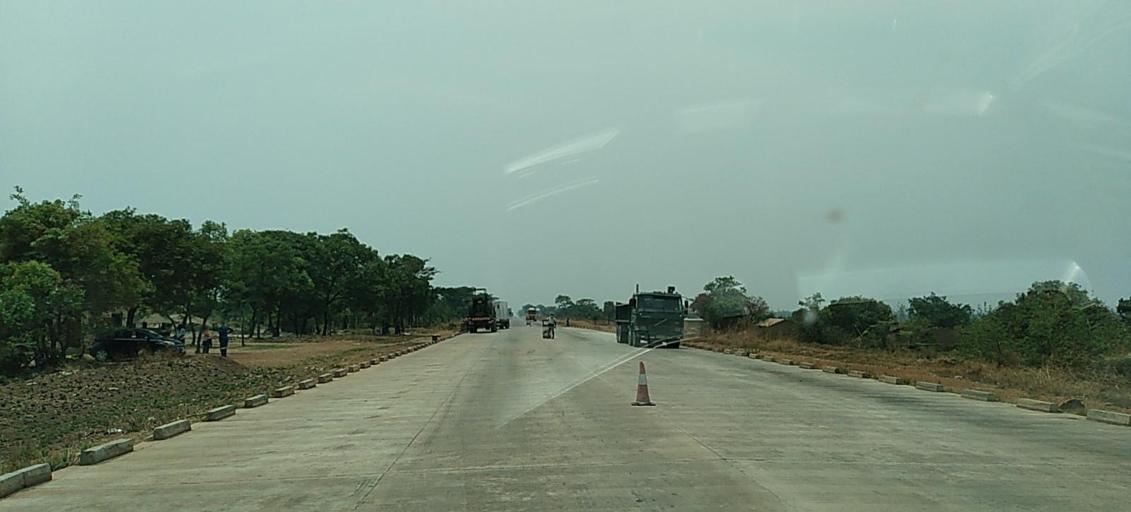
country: CD
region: Katanga
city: Kipushi
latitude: -12.3373
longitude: 27.0757
